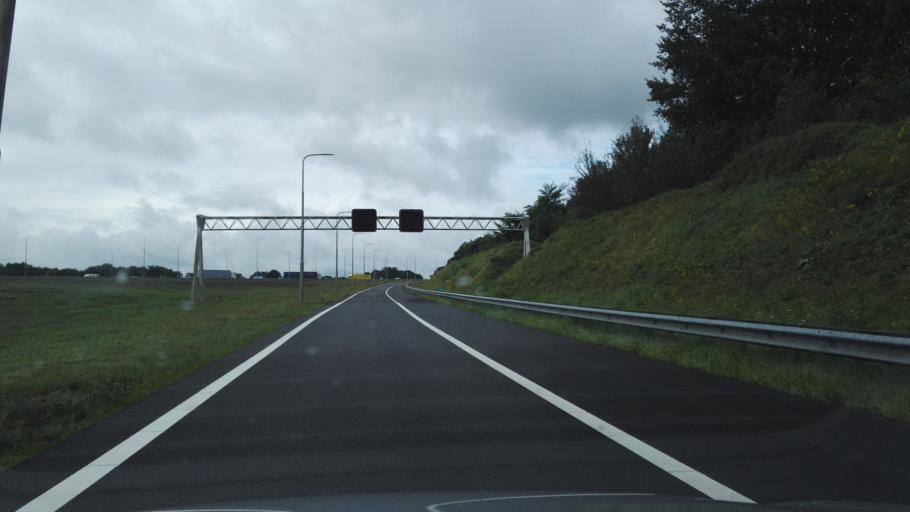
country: NL
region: Gelderland
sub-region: Gemeente Apeldoorn
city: Apeldoorn
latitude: 52.1891
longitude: 6.0192
